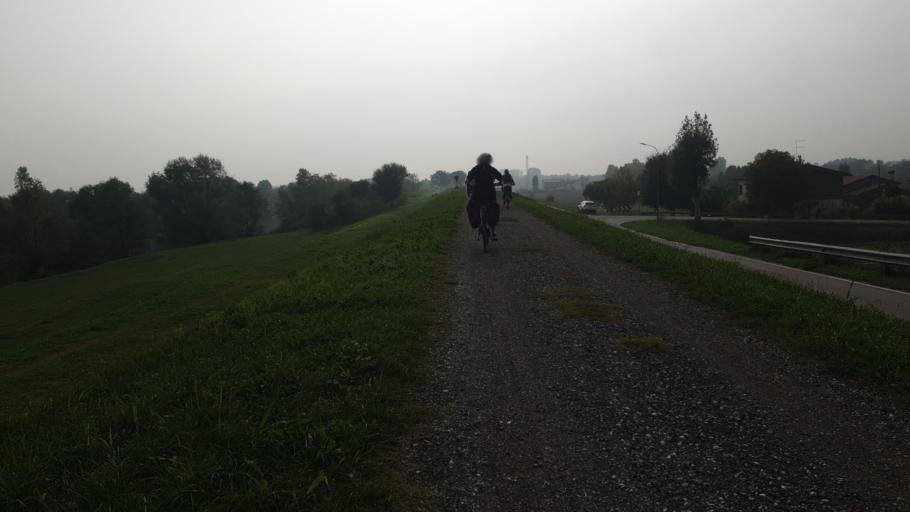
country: IT
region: Veneto
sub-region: Provincia di Venezia
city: Campolongo Maggiore
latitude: 45.3377
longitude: 12.0564
